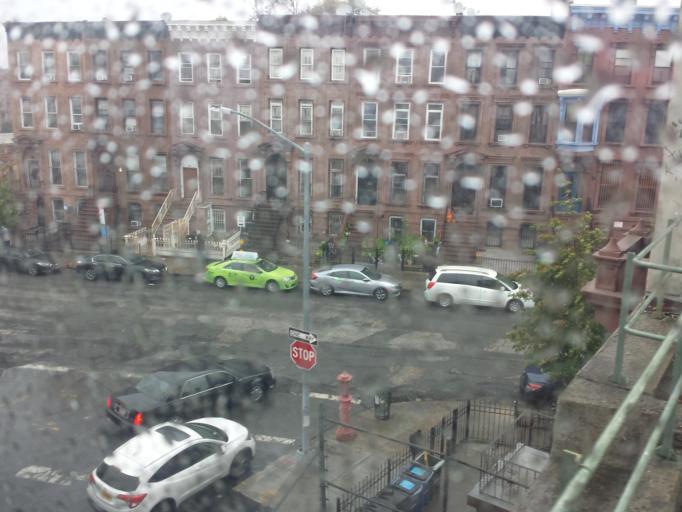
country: US
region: New York
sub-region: Kings County
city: Brooklyn
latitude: 40.6801
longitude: -73.9559
